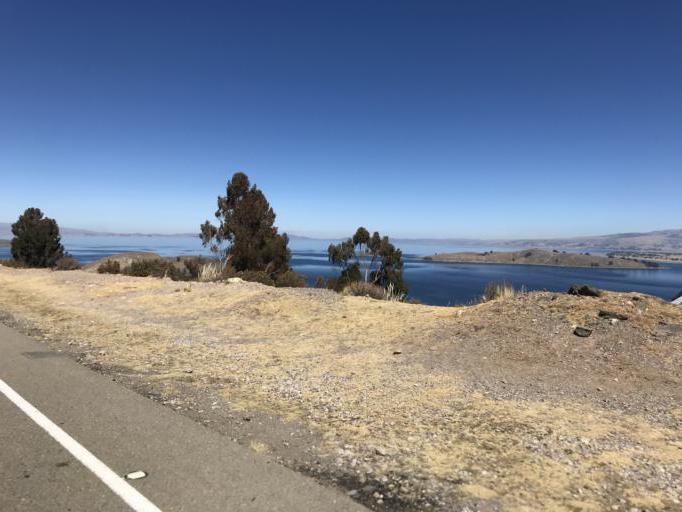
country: BO
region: La Paz
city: San Pedro
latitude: -16.1940
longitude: -68.9145
